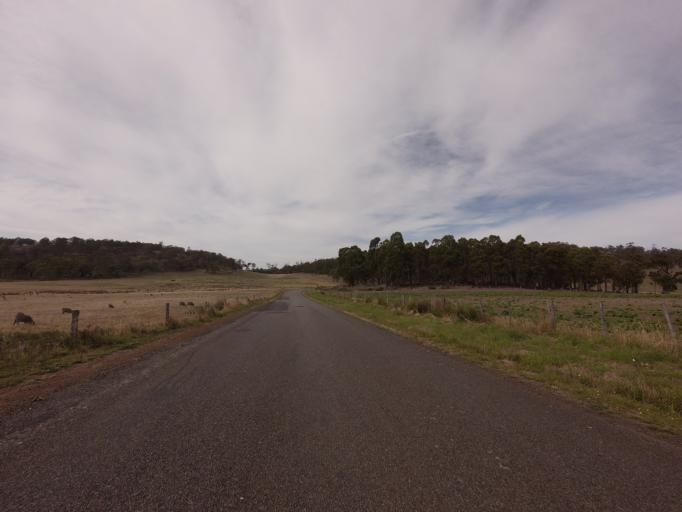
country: AU
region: Tasmania
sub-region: Sorell
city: Sorell
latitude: -42.5276
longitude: 147.6518
